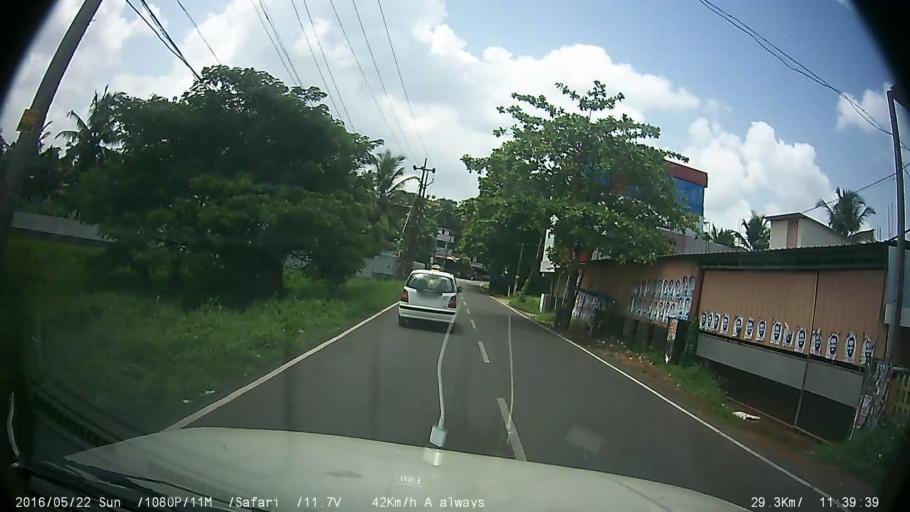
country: IN
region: Kerala
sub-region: Kottayam
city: Kottayam
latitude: 9.5592
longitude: 76.5159
